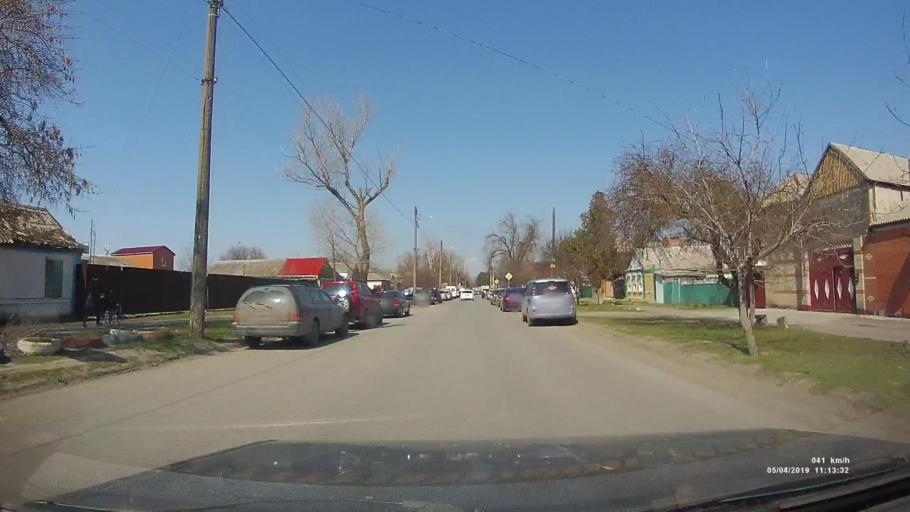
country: RU
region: Rostov
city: Azov
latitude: 47.1026
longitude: 39.4308
